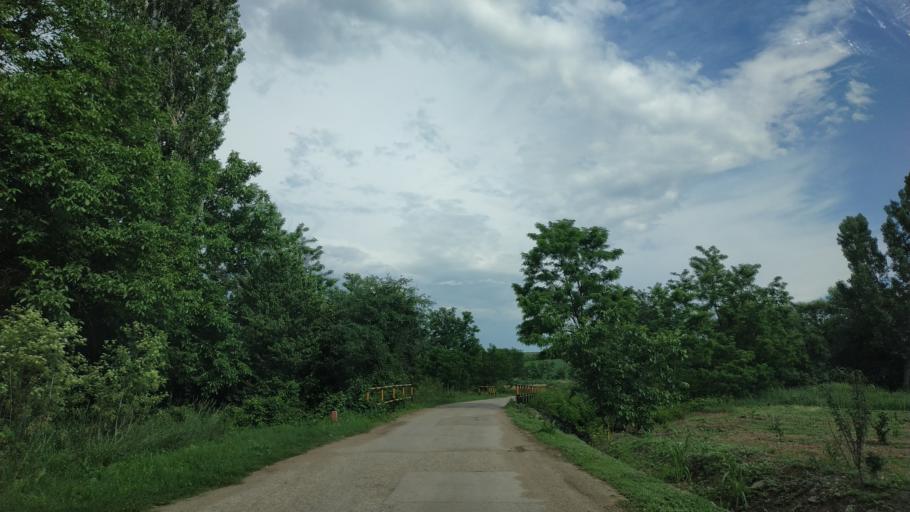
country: RS
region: Central Serbia
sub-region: Nisavski Okrug
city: Aleksinac
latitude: 43.6139
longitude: 21.6473
